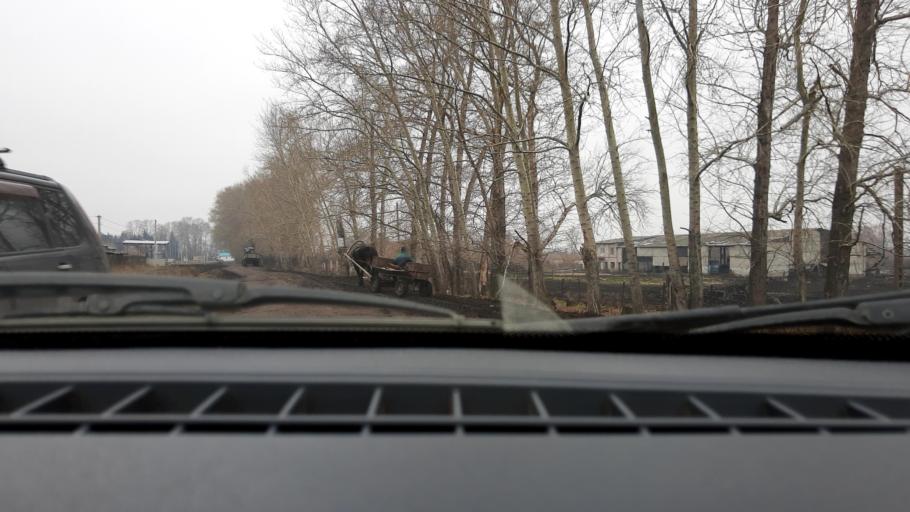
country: RU
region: Bashkortostan
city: Mikhaylovka
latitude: 54.8584
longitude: 55.8185
